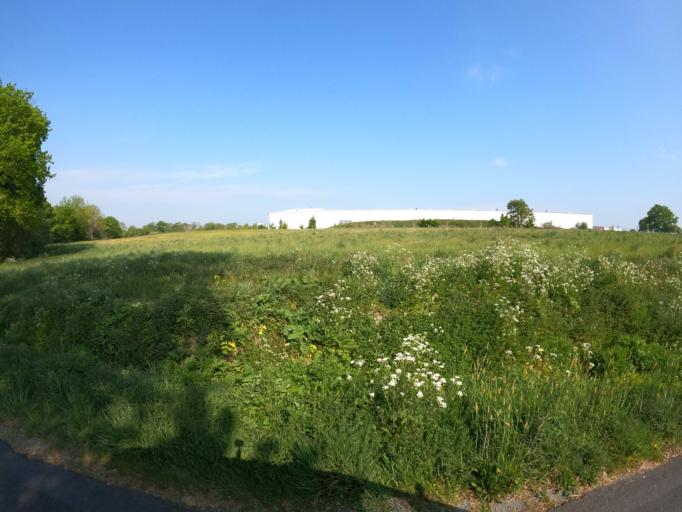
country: FR
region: Pays de la Loire
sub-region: Departement de la Vendee
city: La Bruffiere
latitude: 47.0056
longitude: -1.1935
